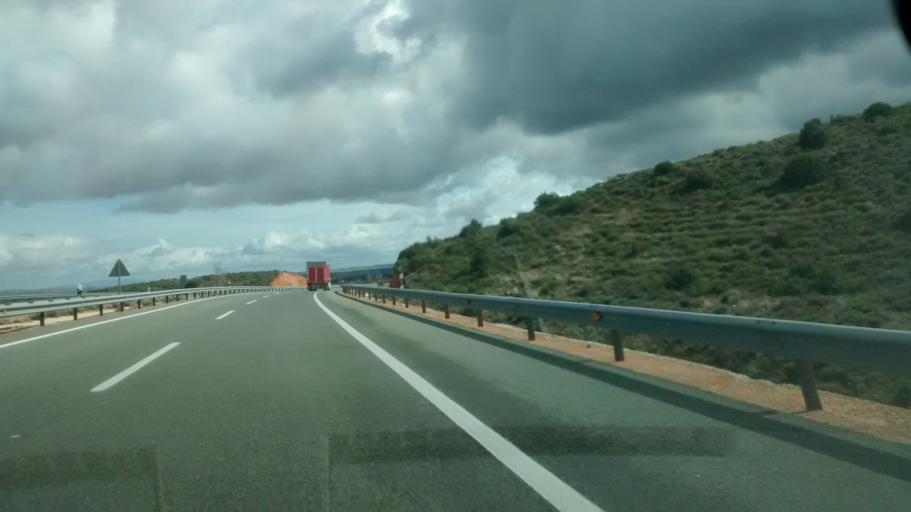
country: ES
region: Castille and Leon
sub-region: Provincia de Soria
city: Arcos de Jalon
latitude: 41.2018
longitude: -2.3263
